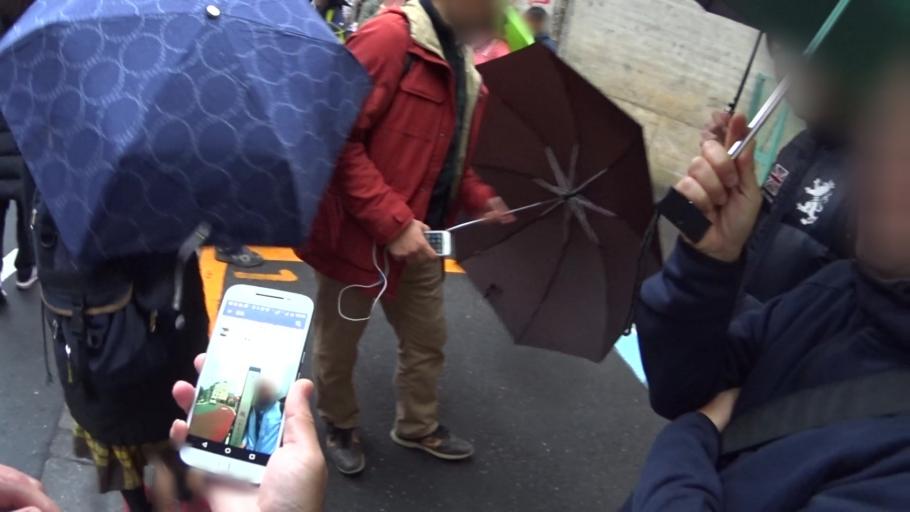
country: JP
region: Tokyo
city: Tokyo
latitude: 35.6910
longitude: 139.7236
